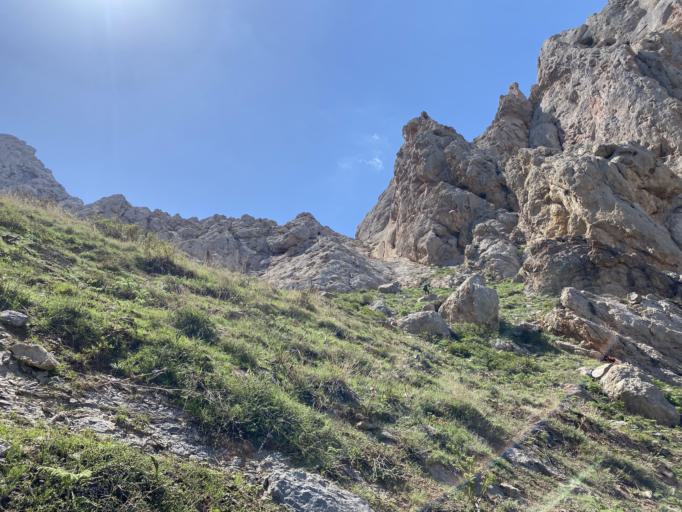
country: KZ
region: Ongtustik Qazaqstan
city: Ashchysay
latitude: 43.7629
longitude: 68.7863
